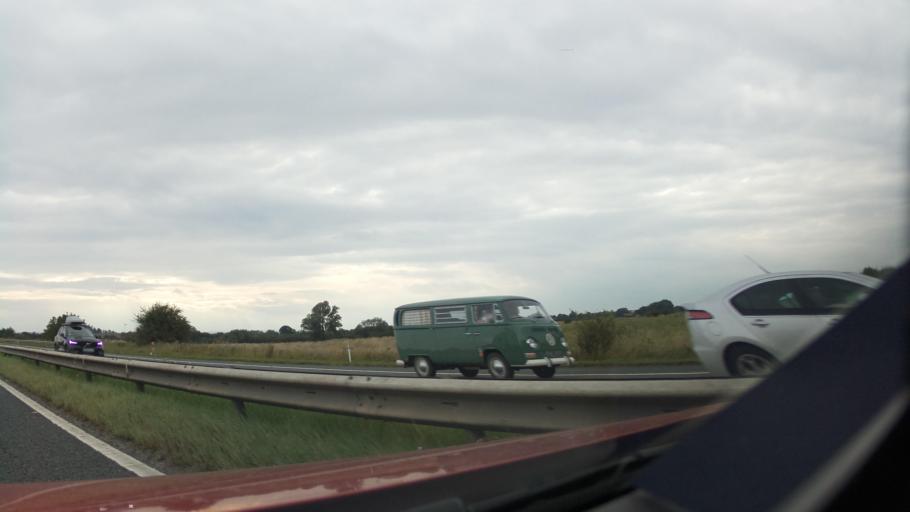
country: GB
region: England
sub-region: Darlington
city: Coatham Mundeville
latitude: 54.5709
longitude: -1.5775
